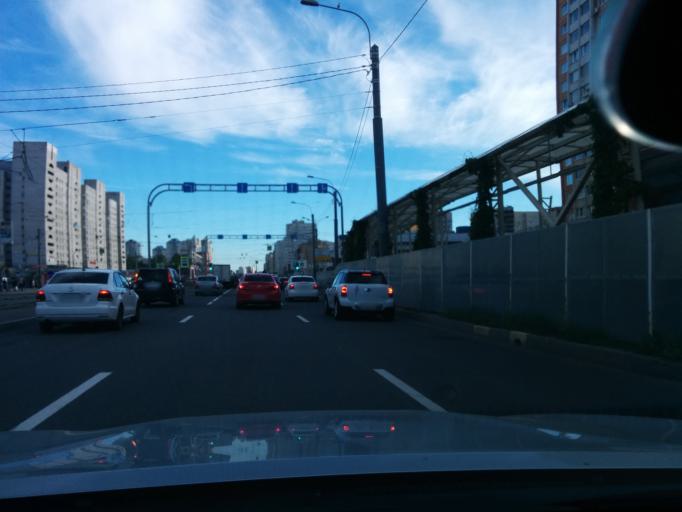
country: RU
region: Leningrad
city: Parnas
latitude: 60.0542
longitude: 30.3357
